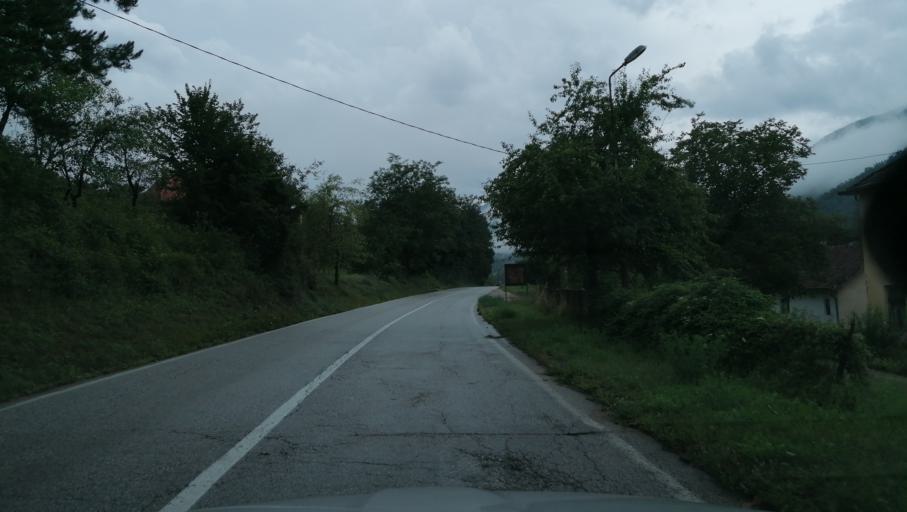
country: RS
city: Durici
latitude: 43.7595
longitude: 19.3858
